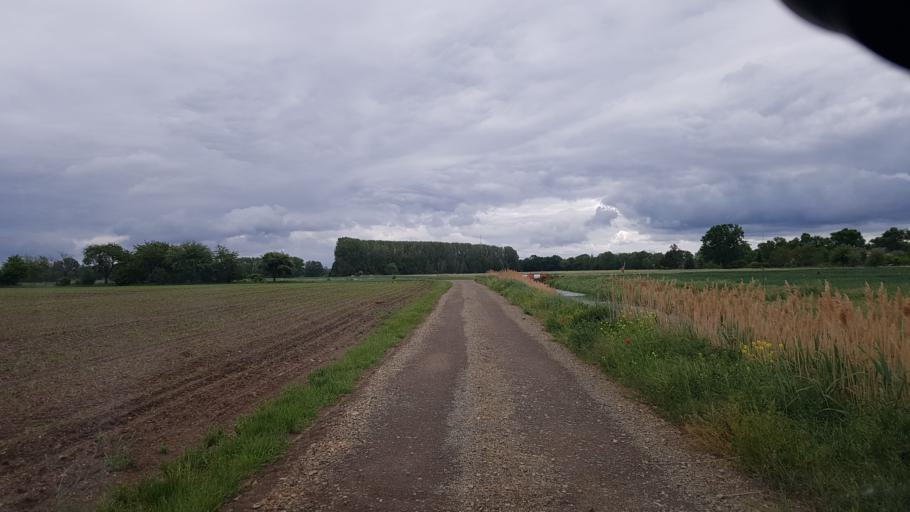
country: DE
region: Brandenburg
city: Doberlug-Kirchhain
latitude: 51.6540
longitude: 13.5492
